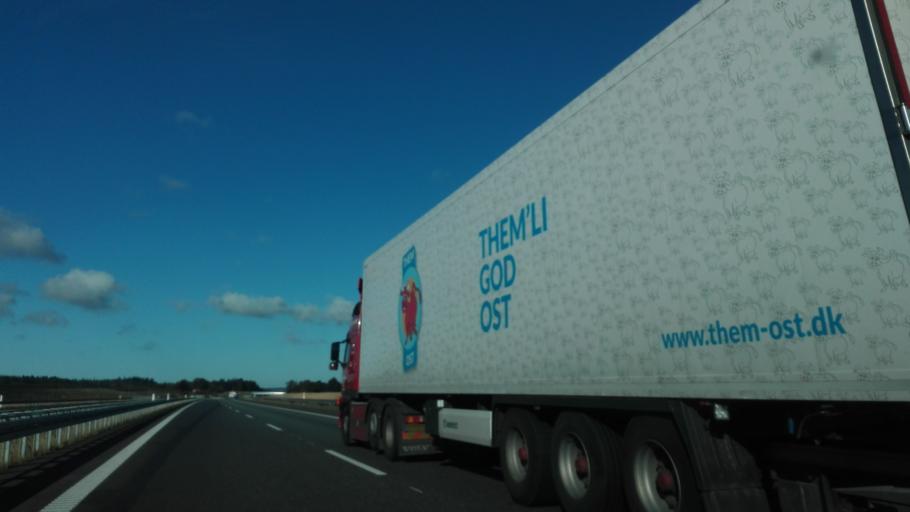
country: DK
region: Central Jutland
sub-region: Silkeborg Kommune
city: Svejbaek
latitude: 56.1516
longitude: 9.6408
